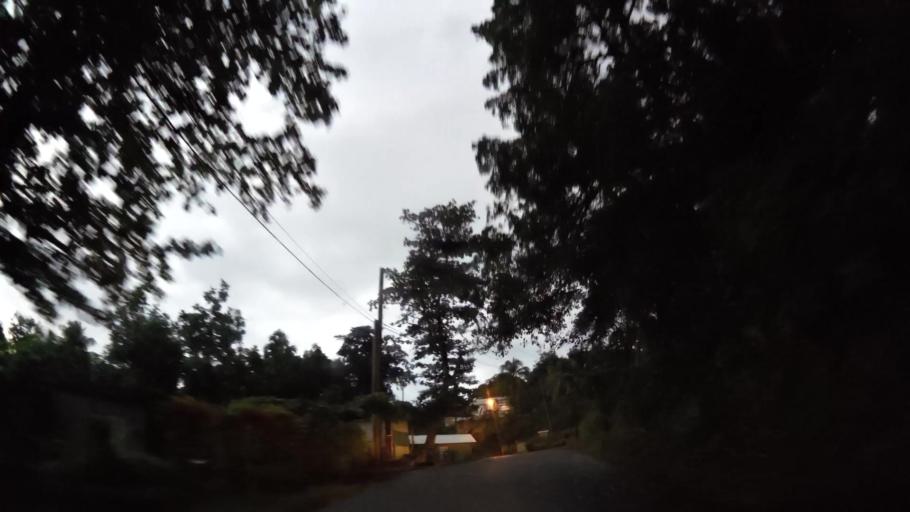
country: DM
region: Saint Andrew
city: Calibishie
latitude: 15.5871
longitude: -61.3298
